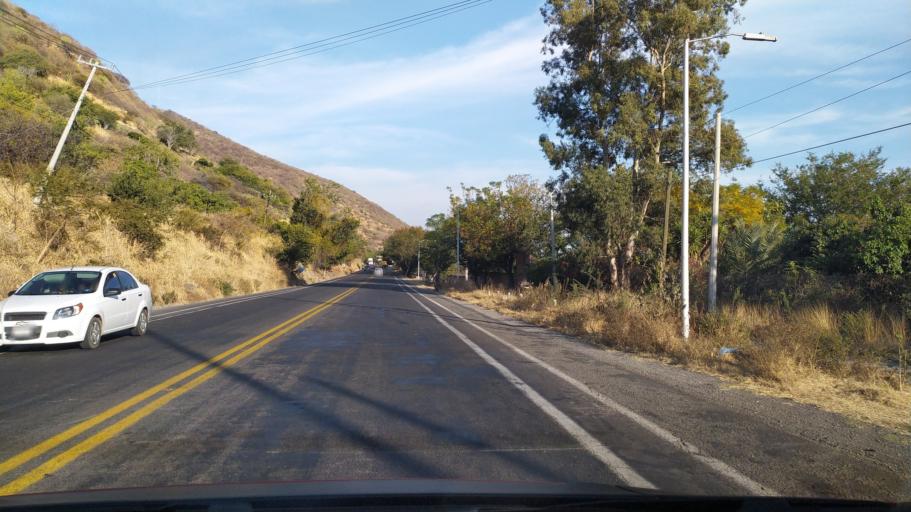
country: MX
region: Jalisco
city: Jamay
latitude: 20.2934
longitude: -102.7430
